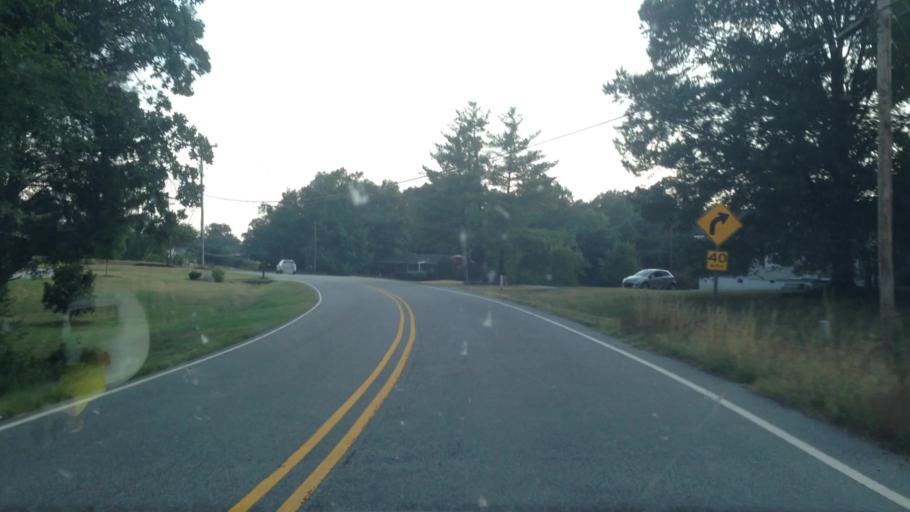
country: US
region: North Carolina
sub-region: Guilford County
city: High Point
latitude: 35.9794
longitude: -80.0710
